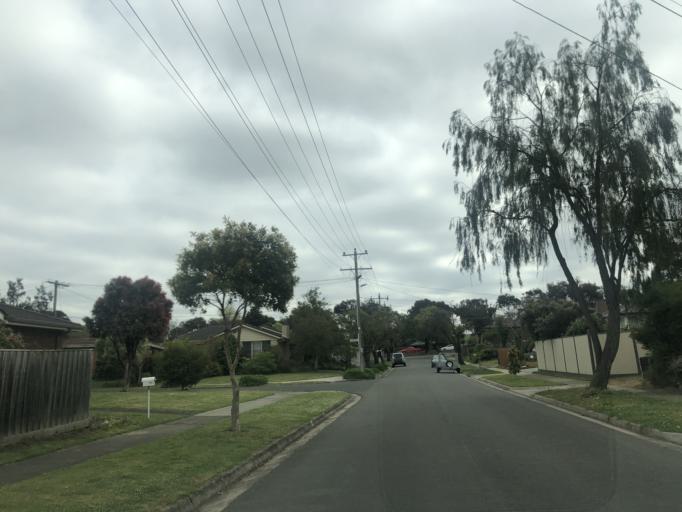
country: AU
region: Victoria
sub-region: Monash
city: Notting Hill
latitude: -37.9063
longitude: 145.1697
